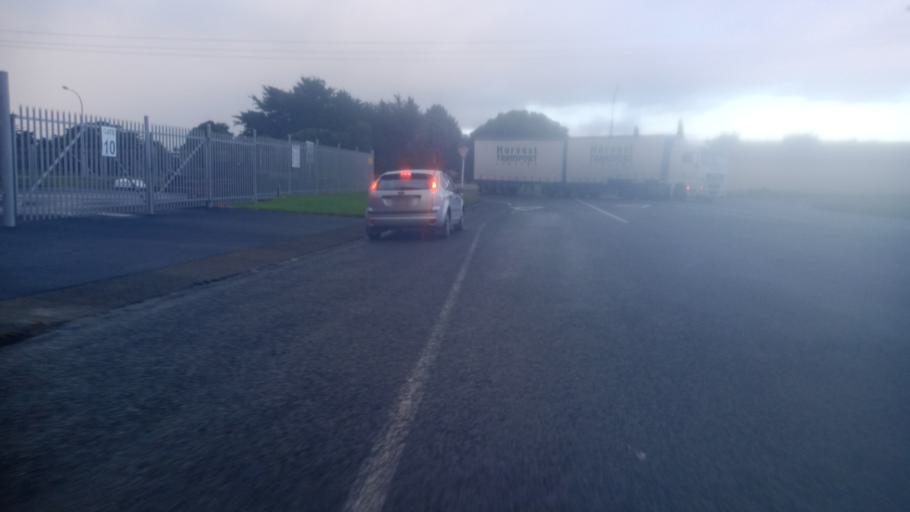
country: NZ
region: Gisborne
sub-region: Gisborne District
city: Gisborne
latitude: -38.6684
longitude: 177.9973
